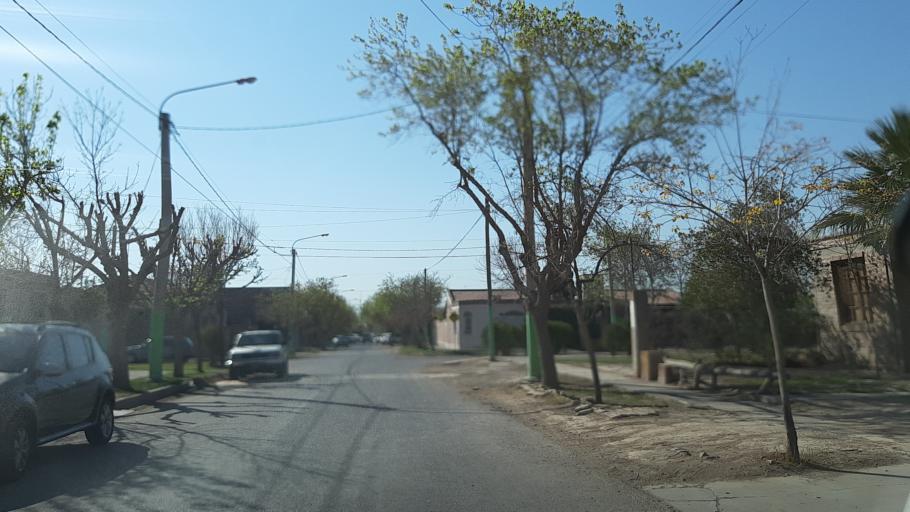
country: AR
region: San Juan
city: San Juan
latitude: -31.5232
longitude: -68.5842
